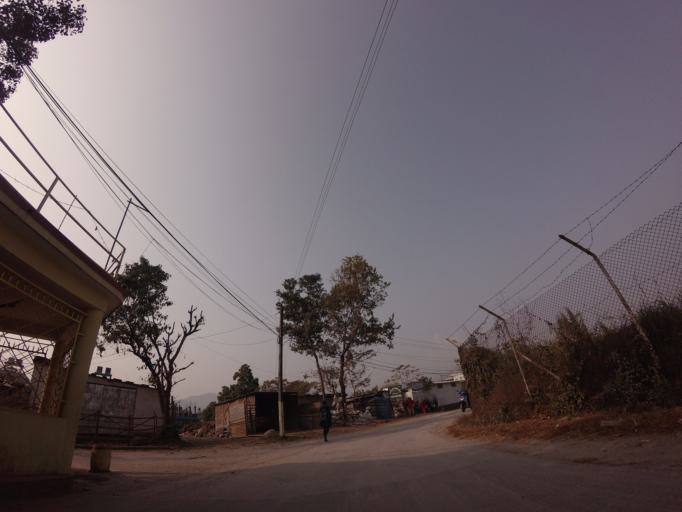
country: NP
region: Western Region
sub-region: Gandaki Zone
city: Pokhara
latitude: 28.1979
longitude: 83.9821
